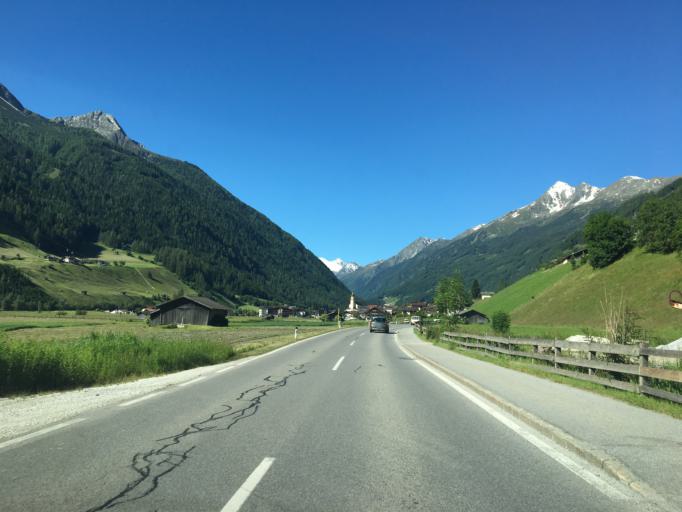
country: AT
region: Tyrol
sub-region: Politischer Bezirk Innsbruck Land
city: Neustift im Stubaital
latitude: 47.1186
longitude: 11.3180
